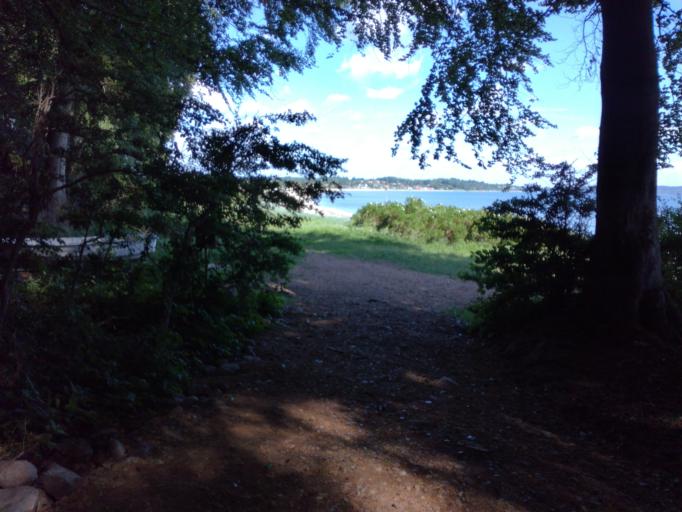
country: DK
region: South Denmark
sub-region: Fredericia Kommune
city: Fredericia
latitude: 55.6237
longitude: 9.7549
